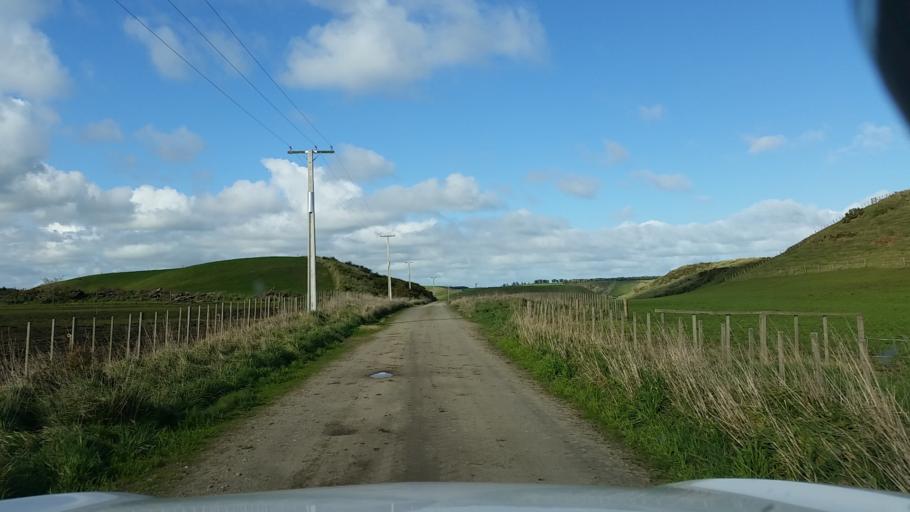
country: NZ
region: Taranaki
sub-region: South Taranaki District
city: Patea
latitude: -39.7183
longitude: 174.4683
